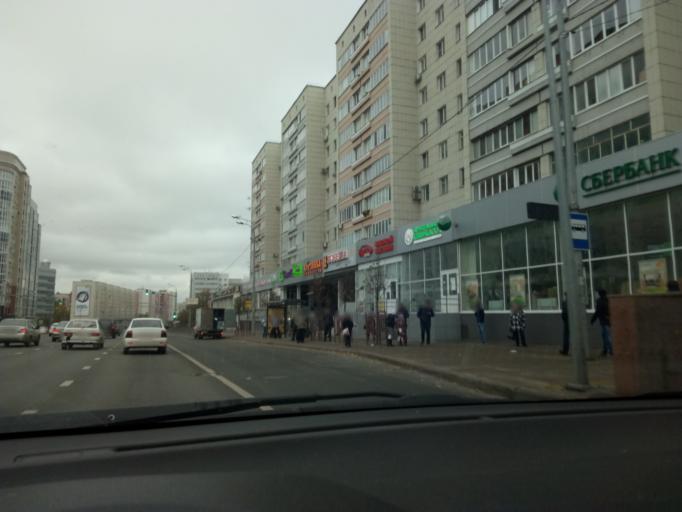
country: RU
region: Tatarstan
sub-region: Gorod Kazan'
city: Kazan
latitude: 55.7893
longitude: 49.1519
